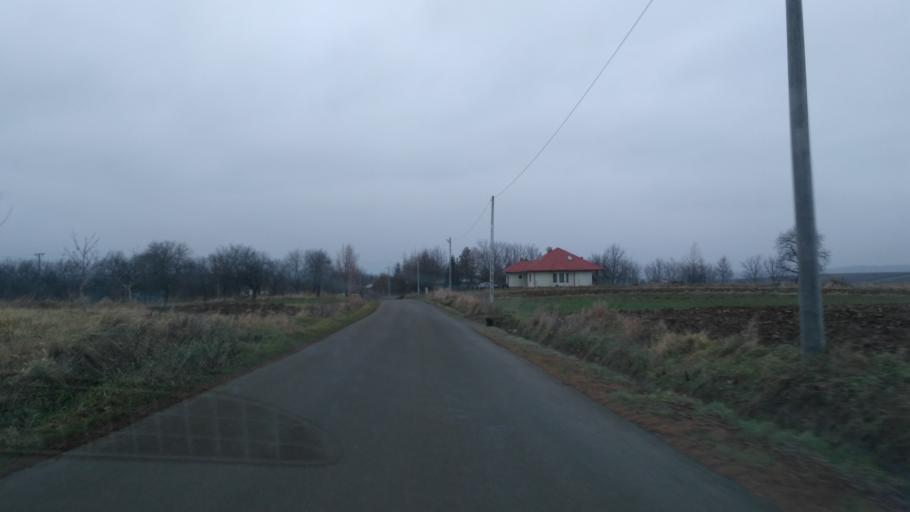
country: PL
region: Subcarpathian Voivodeship
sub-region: Powiat jaroslawski
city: Pruchnik
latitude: 49.9206
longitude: 22.5350
